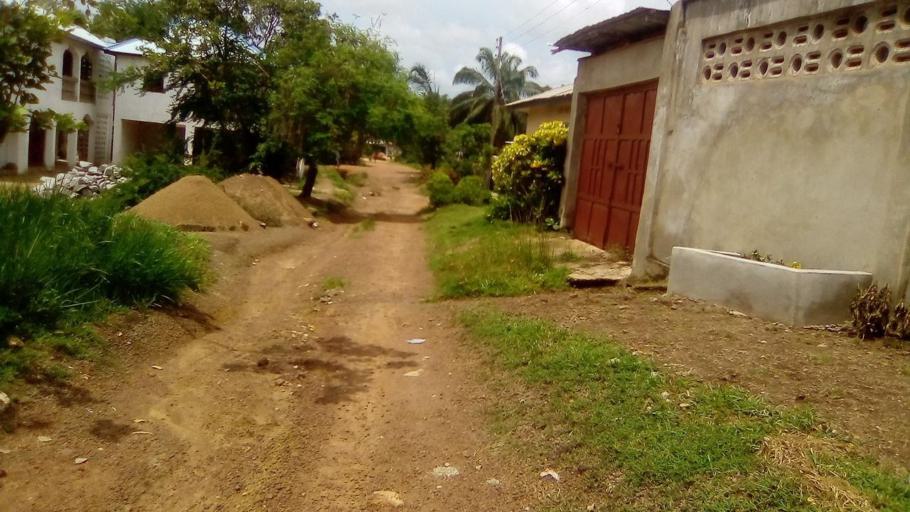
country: SL
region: Southern Province
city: Bo
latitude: 7.9386
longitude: -11.7345
